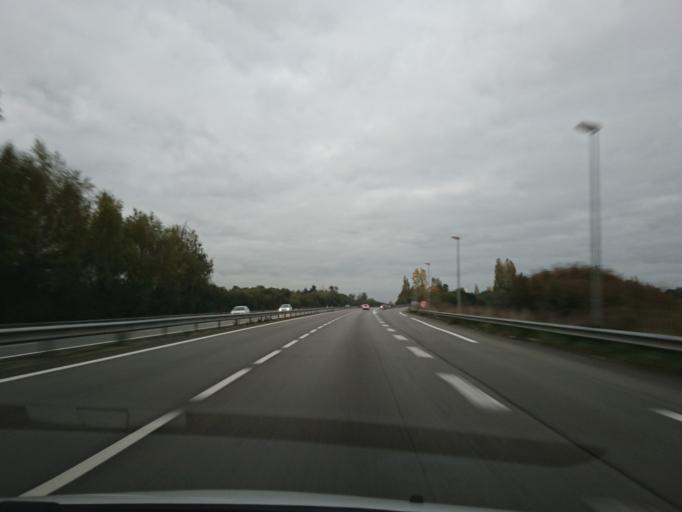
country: FR
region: Pays de la Loire
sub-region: Departement de la Loire-Atlantique
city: Treillieres
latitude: 47.3328
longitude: -1.6519
